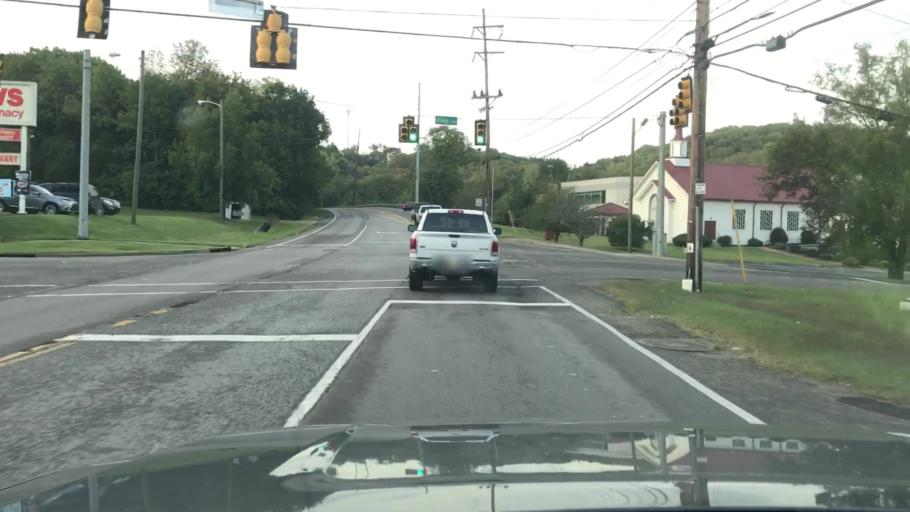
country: US
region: Tennessee
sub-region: Davidson County
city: Nashville
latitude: 36.2183
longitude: -86.8371
